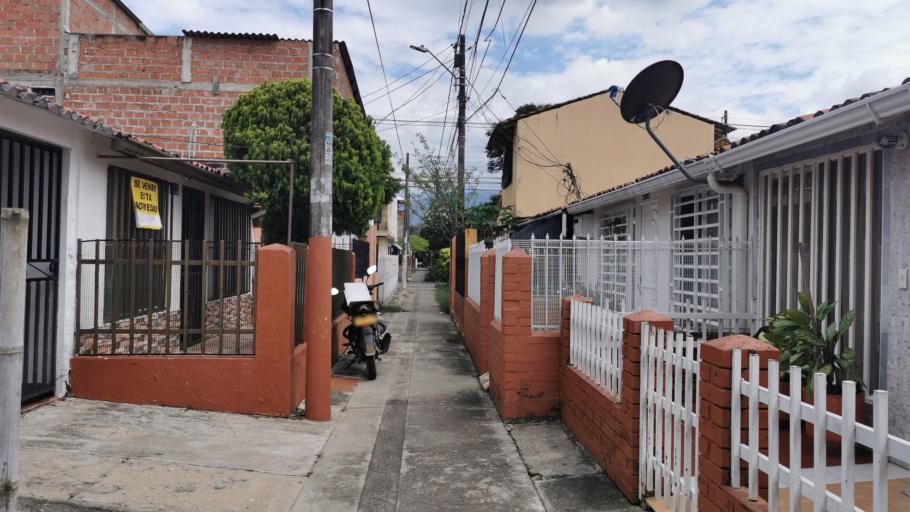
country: CO
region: Valle del Cauca
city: Jamundi
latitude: 3.2655
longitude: -76.5357
